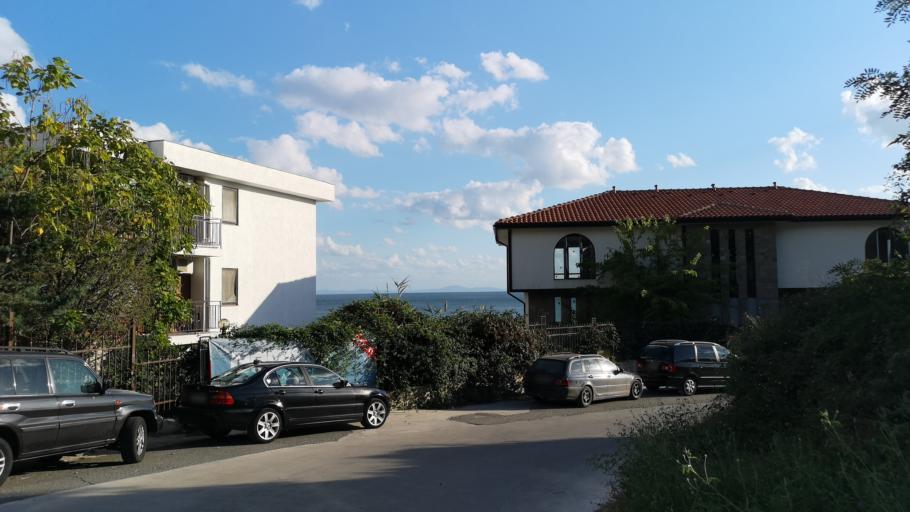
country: BG
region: Burgas
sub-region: Obshtina Nesebur
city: Sveti Vlas
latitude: 42.7040
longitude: 27.8049
